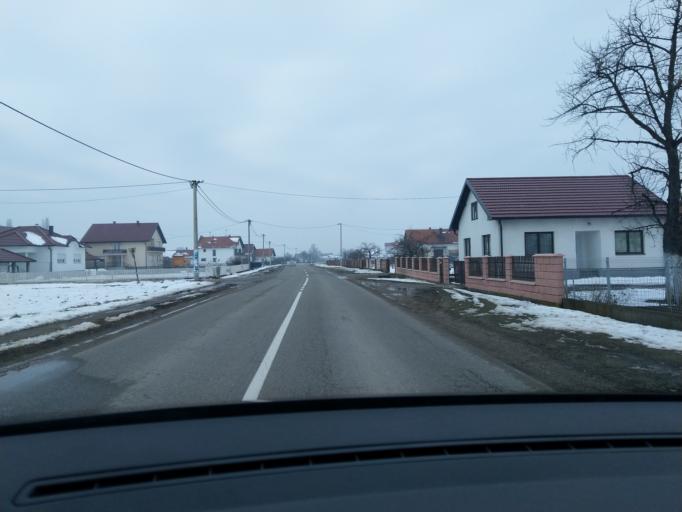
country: BA
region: Republika Srpska
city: Velika Obarska
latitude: 44.7895
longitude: 19.1824
